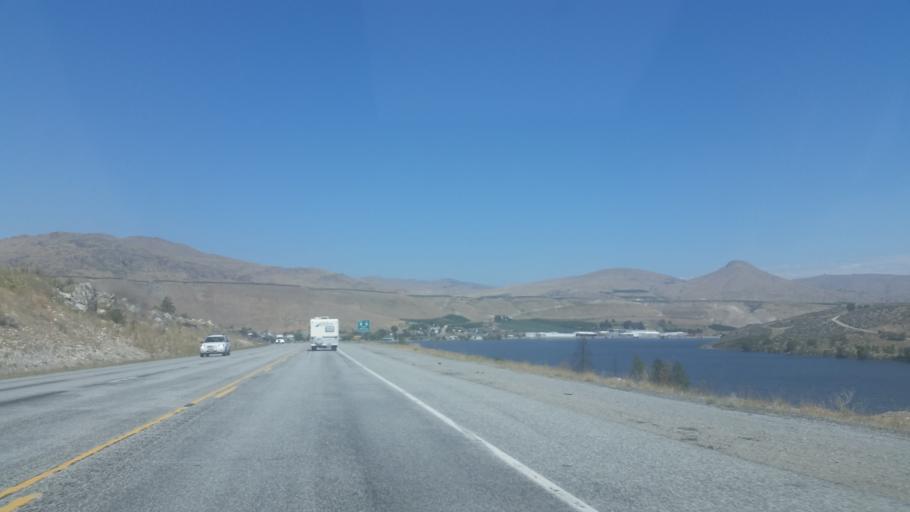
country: US
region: Washington
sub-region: Okanogan County
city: Brewster
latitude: 48.0401
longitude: -119.8961
